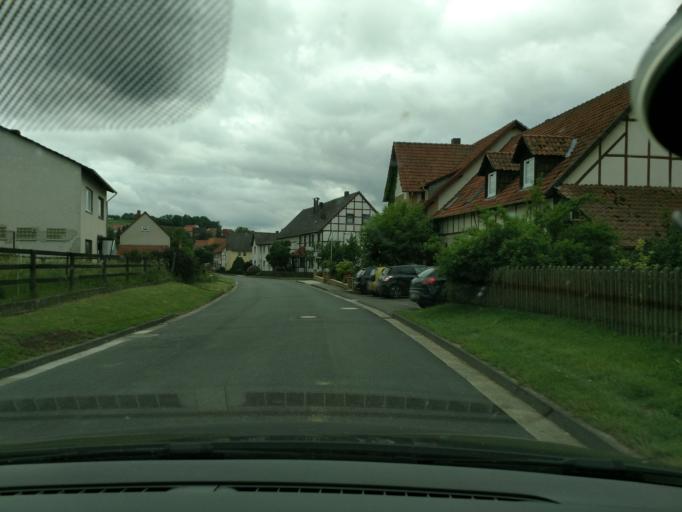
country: DE
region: Hesse
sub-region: Regierungsbezirk Kassel
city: Volkmarsen
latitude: 51.3490
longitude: 9.0870
